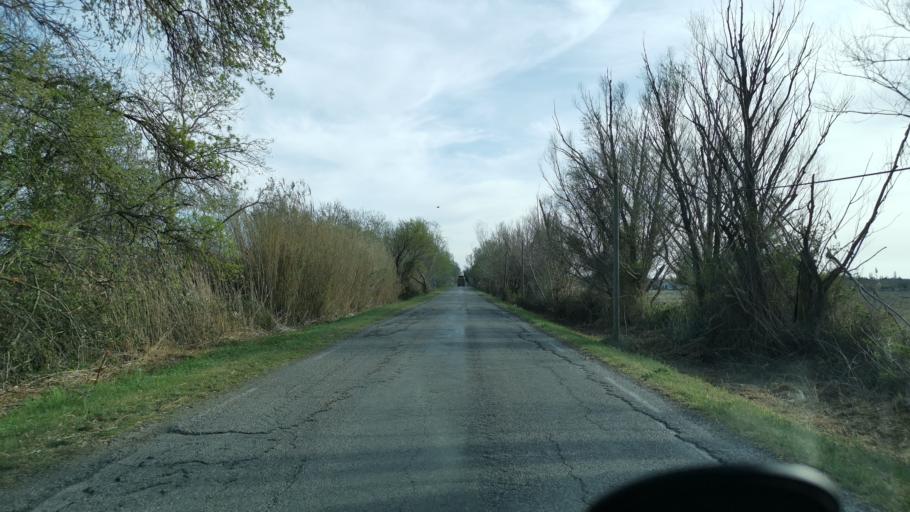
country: FR
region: Provence-Alpes-Cote d'Azur
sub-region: Departement des Bouches-du-Rhone
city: Arles
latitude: 43.6252
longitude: 4.7120
